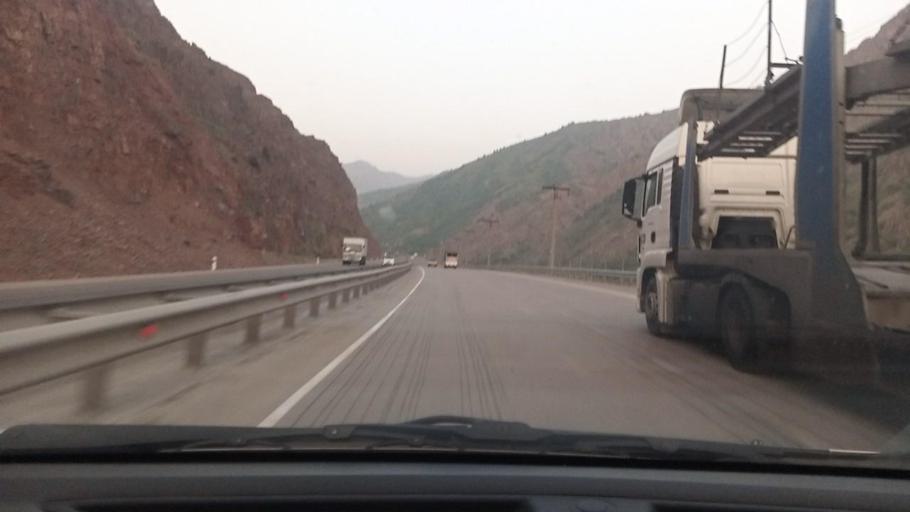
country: UZ
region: Toshkent
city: Angren
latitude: 41.1403
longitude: 70.3921
